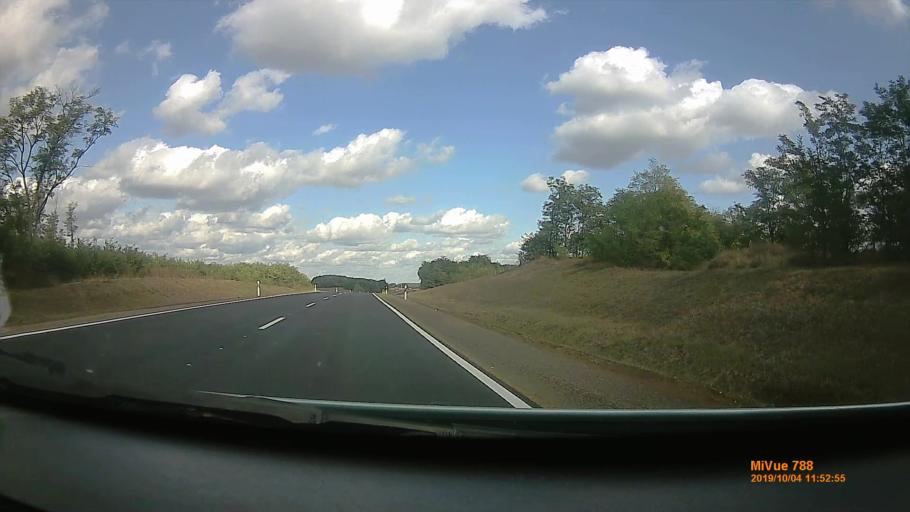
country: HU
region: Szabolcs-Szatmar-Bereg
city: Nyirtelek
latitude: 48.0035
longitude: 21.6734
